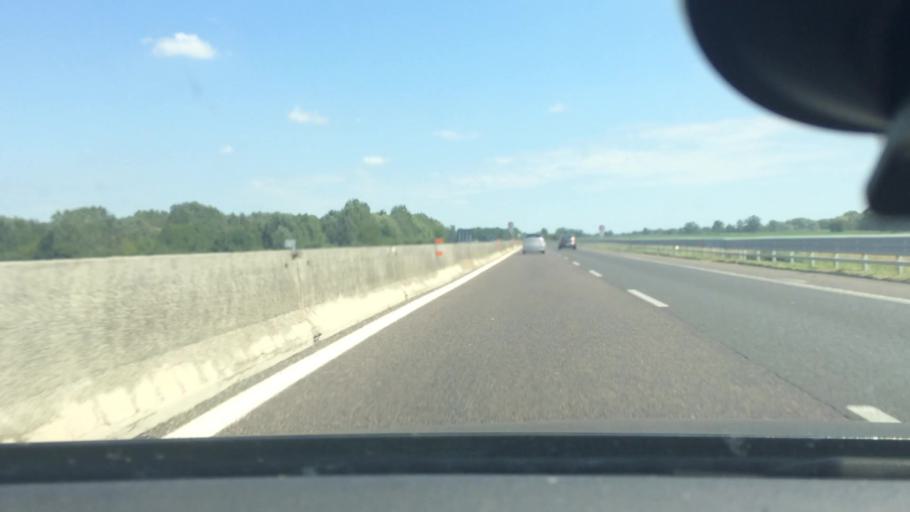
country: IT
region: Emilia-Romagna
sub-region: Provincia di Bologna
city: Altedo
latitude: 44.7057
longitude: 11.4941
